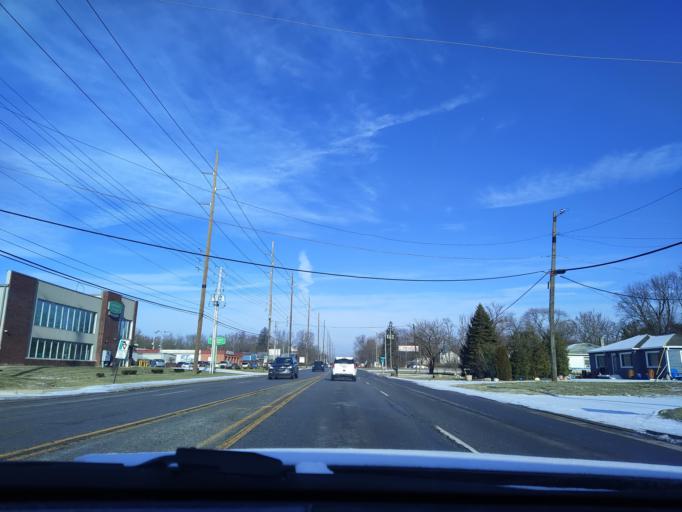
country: US
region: Indiana
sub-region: Marion County
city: Meridian Hills
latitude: 39.8868
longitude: -86.2107
